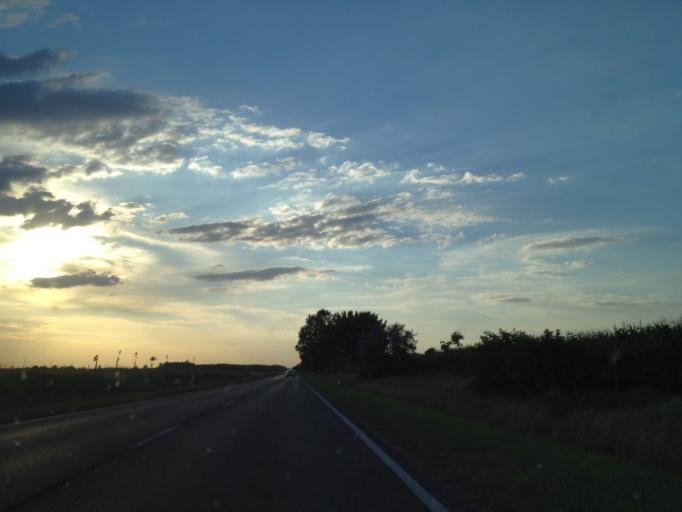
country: HU
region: Gyor-Moson-Sopron
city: Otteveny
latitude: 47.7426
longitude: 17.4651
